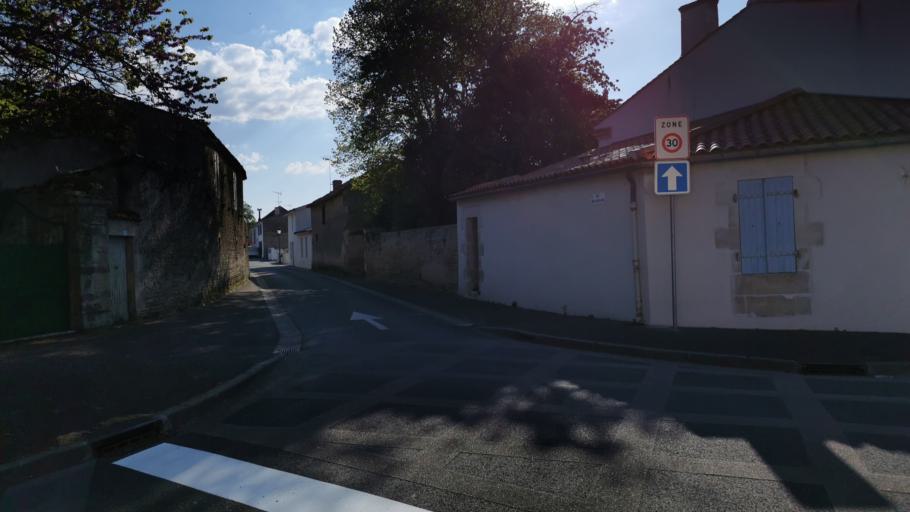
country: FR
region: Pays de la Loire
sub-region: Departement de la Vendee
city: Triaize
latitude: 46.3543
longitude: -1.2515
